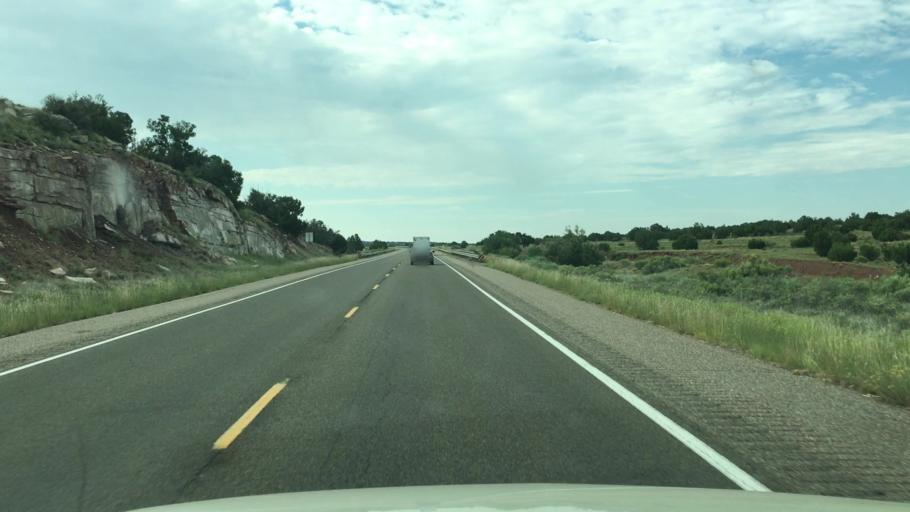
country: US
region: New Mexico
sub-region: Santa Fe County
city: Eldorado at Santa Fe
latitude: 35.2975
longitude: -105.8265
